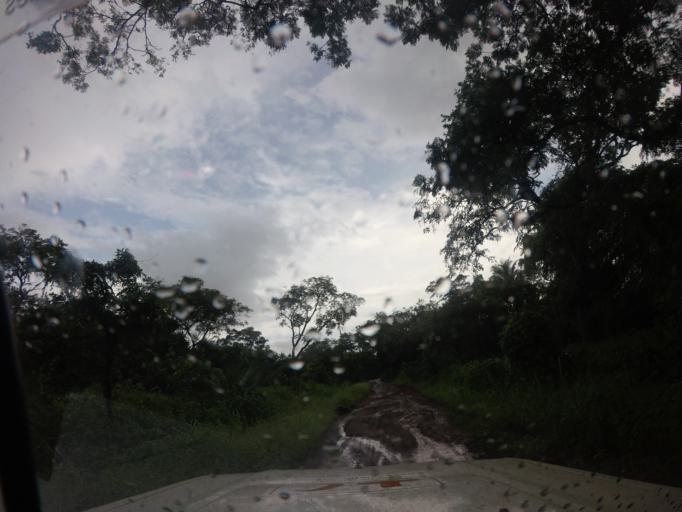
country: SL
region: Northern Province
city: Kamakwie
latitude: 9.7540
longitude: -12.3207
